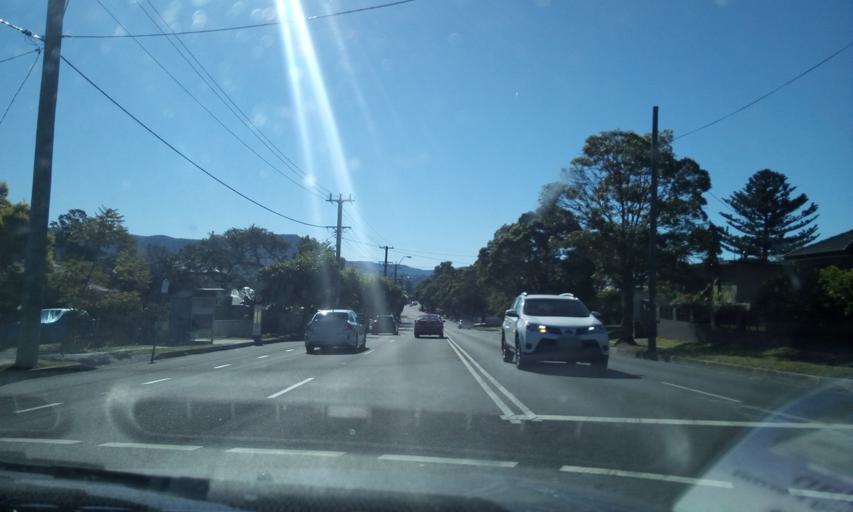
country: AU
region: New South Wales
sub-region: Wollongong
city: Dapto
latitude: -34.5024
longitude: 150.7890
